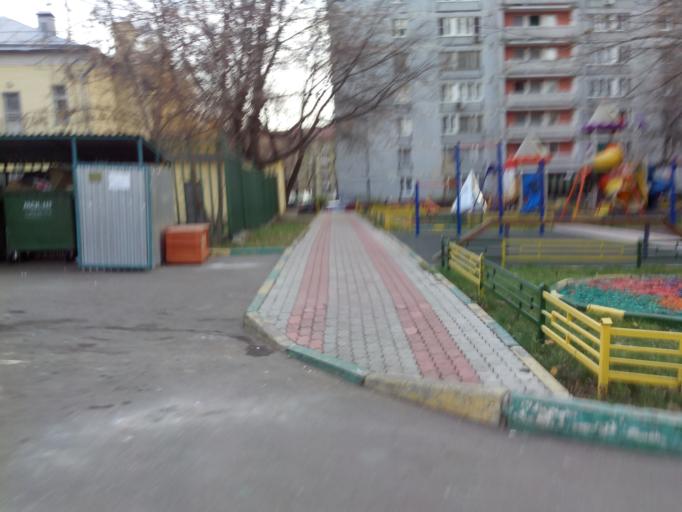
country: RU
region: Moscow
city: Lefortovo
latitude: 55.7658
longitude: 37.7160
